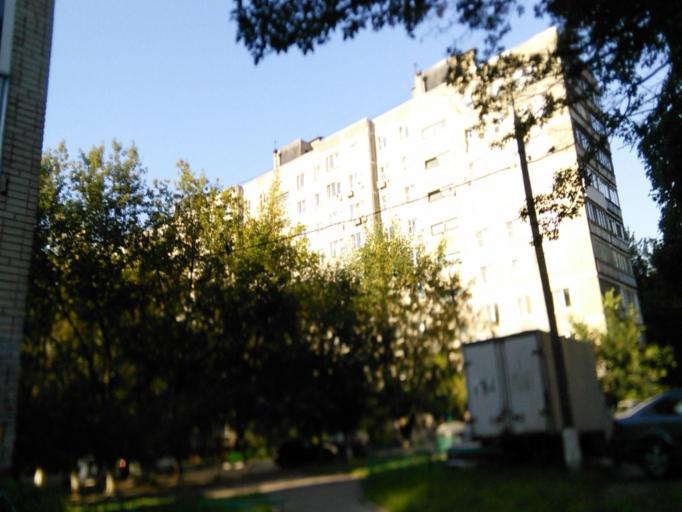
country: RU
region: Moskovskaya
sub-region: Podol'skiy Rayon
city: Podol'sk
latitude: 55.4418
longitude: 37.5655
